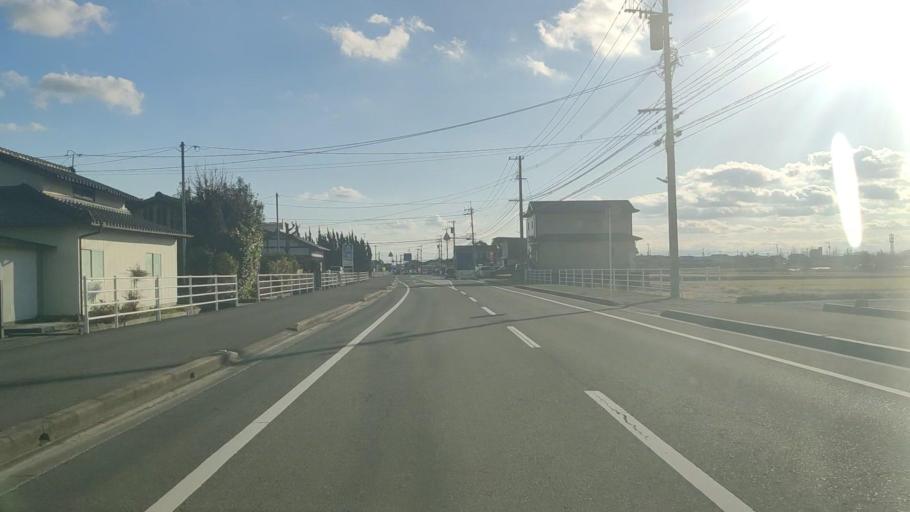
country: JP
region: Saga Prefecture
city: Saga-shi
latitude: 33.3126
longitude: 130.2653
